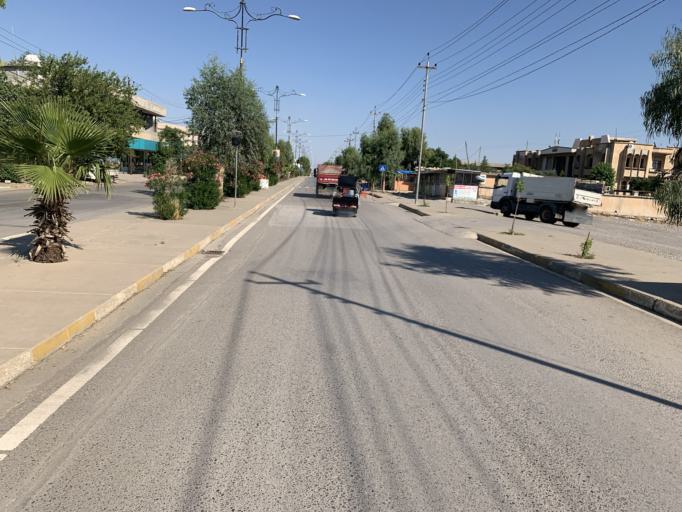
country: IQ
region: As Sulaymaniyah
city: Raniye
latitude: 36.2325
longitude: 44.7891
